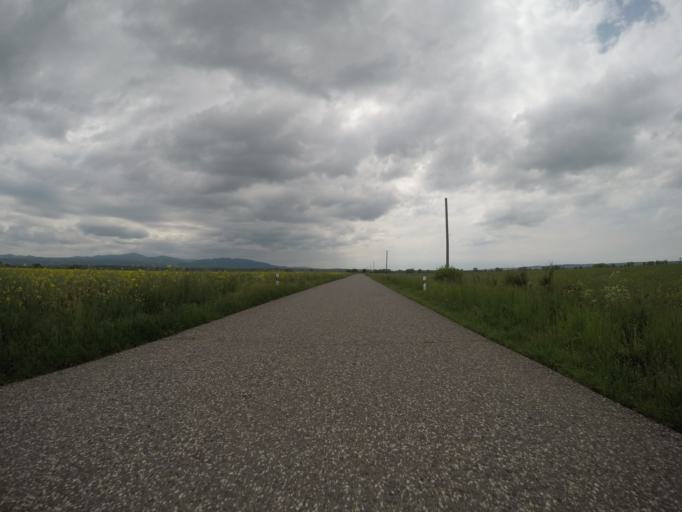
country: SK
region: Nitriansky
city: Sahy
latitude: 48.0725
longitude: 18.8608
